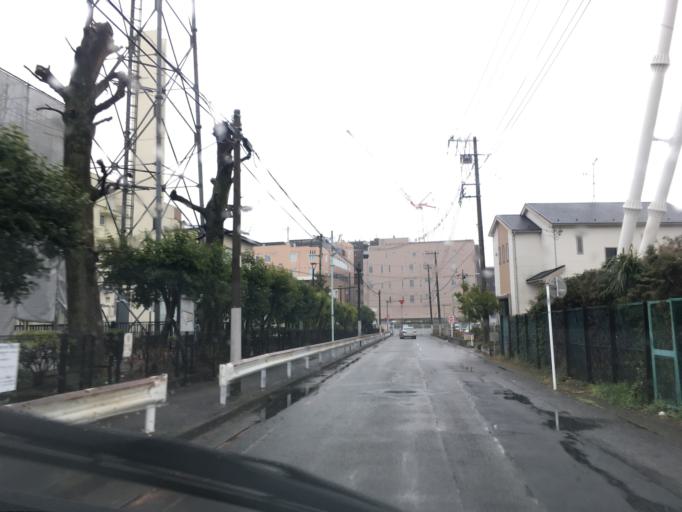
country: JP
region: Saitama
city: Koshigaya
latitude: 35.8928
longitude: 139.7900
